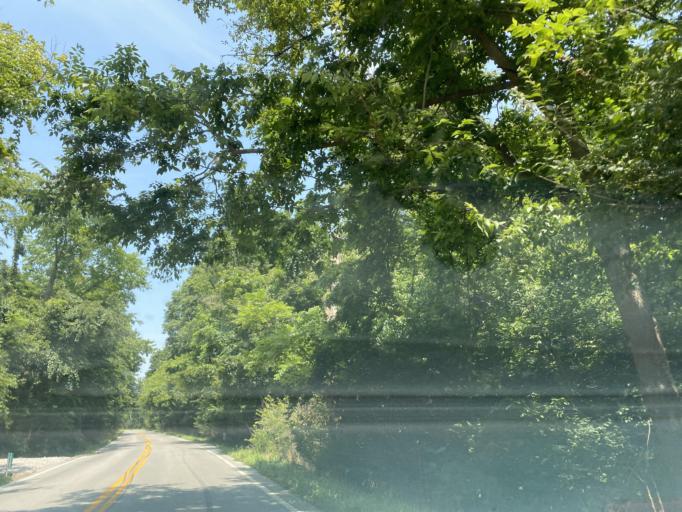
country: US
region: Kentucky
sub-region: Campbell County
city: Claryville
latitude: 38.9032
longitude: -84.4453
